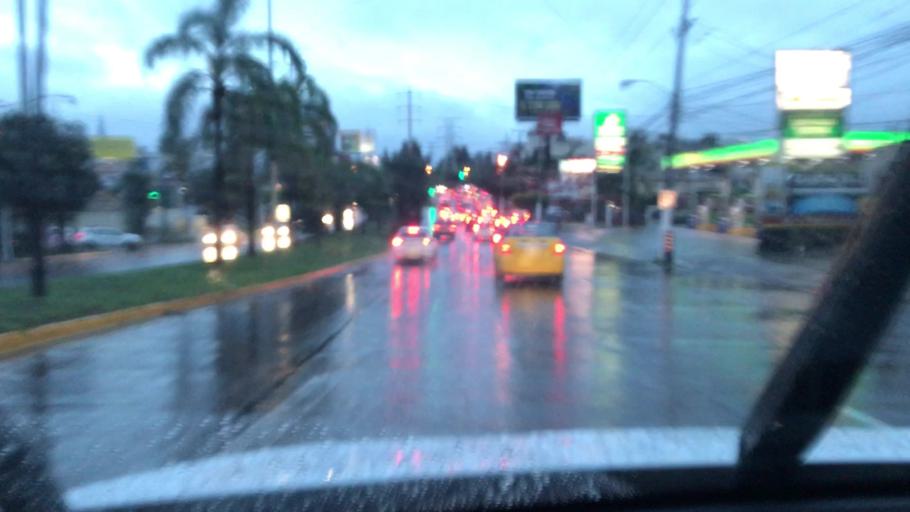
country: MX
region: Jalisco
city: Guadalajara
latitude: 20.6854
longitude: -103.4203
